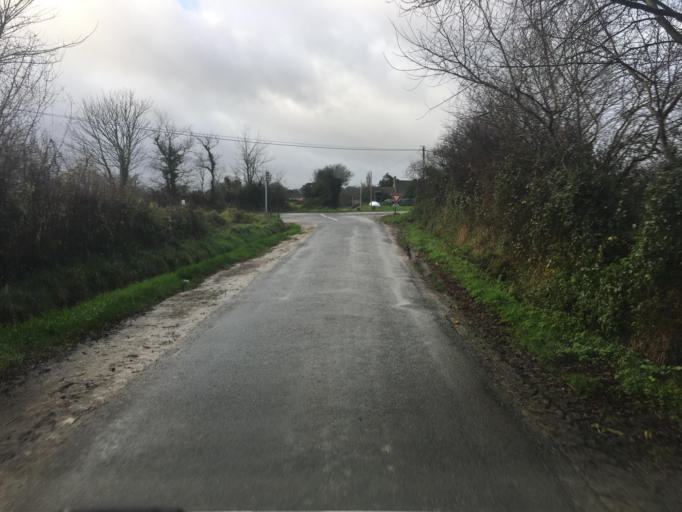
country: FR
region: Lower Normandy
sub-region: Departement de la Manche
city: Saint-Pierre-Eglise
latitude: 49.6710
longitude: -1.3243
